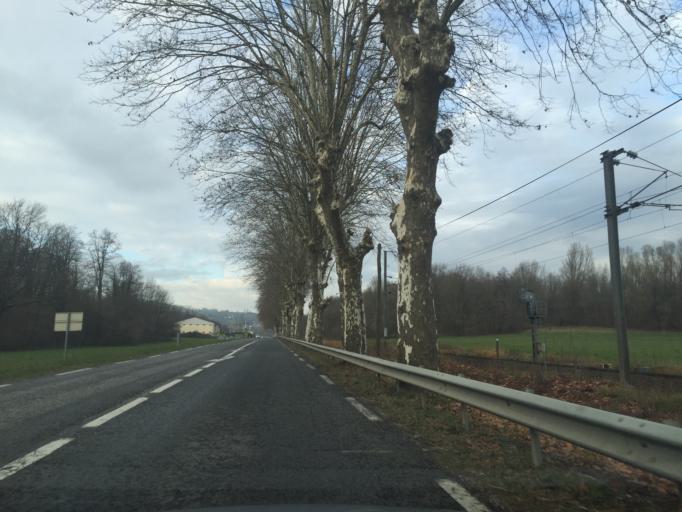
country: FR
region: Rhone-Alpes
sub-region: Departement de la Savoie
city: Gresy-sur-Aix
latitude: 45.7303
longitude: 5.9216
